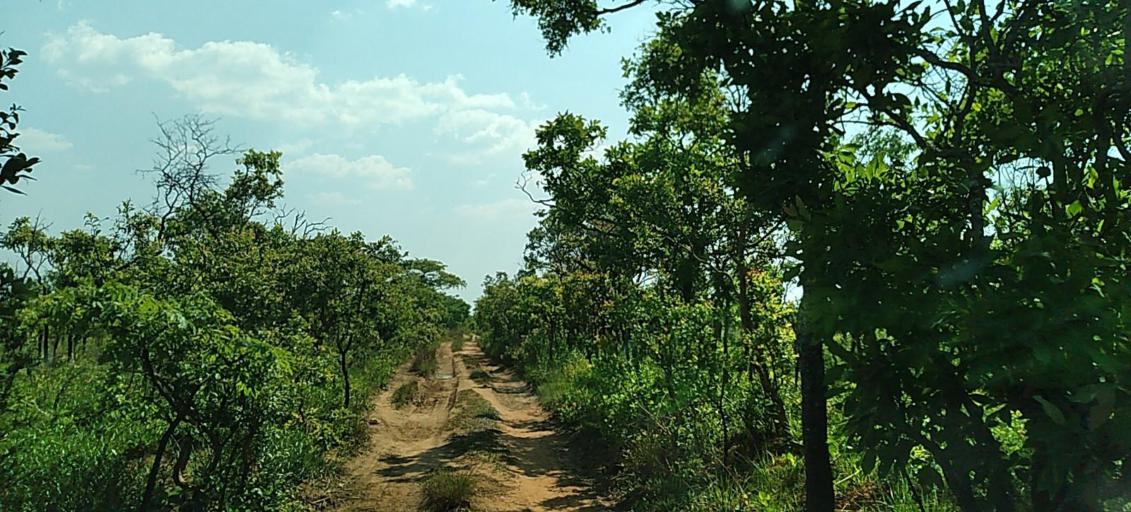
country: CD
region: Katanga
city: Kolwezi
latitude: -11.2691
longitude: 24.9941
